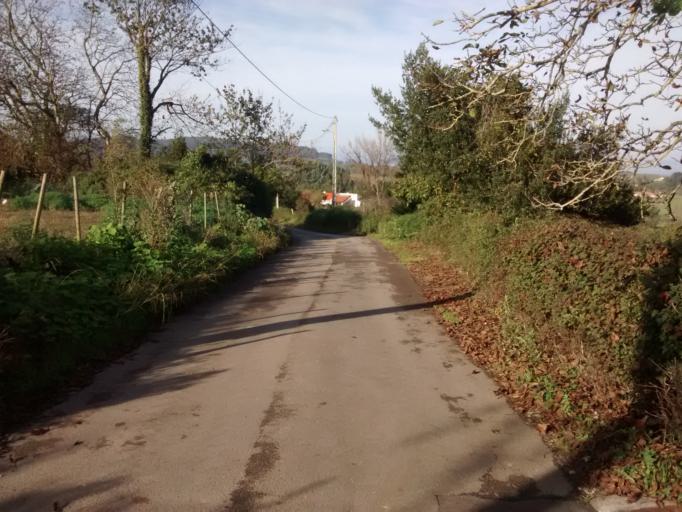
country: ES
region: Asturias
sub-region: Province of Asturias
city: Colunga
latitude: 43.4710
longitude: -5.2385
